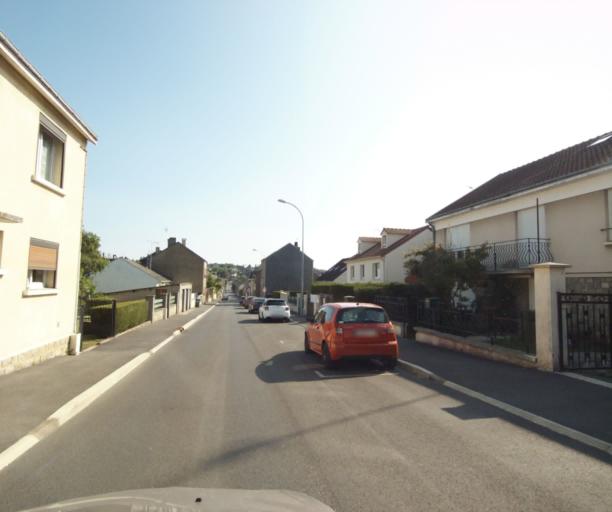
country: FR
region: Champagne-Ardenne
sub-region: Departement des Ardennes
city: Charleville-Mezieres
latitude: 49.7775
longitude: 4.7072
